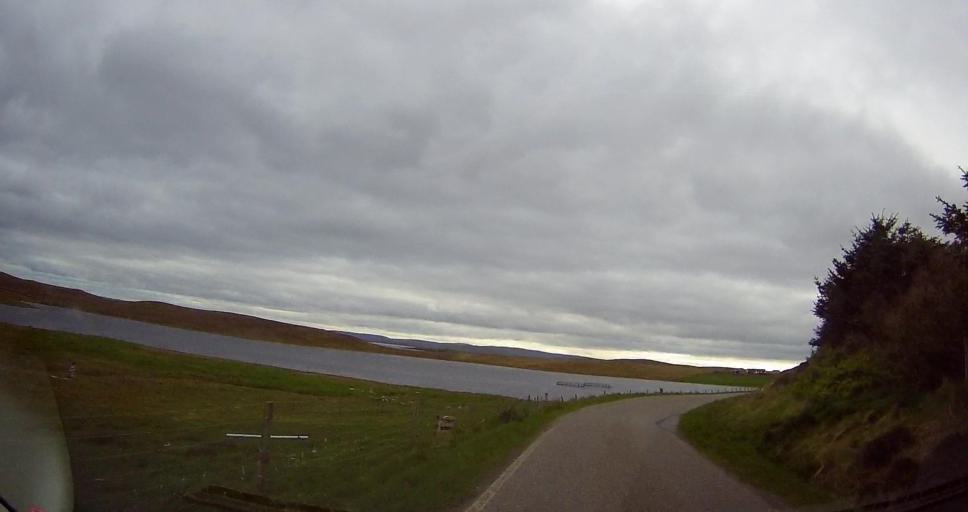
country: GB
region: Scotland
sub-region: Shetland Islands
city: Shetland
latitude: 60.5006
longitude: -1.0670
